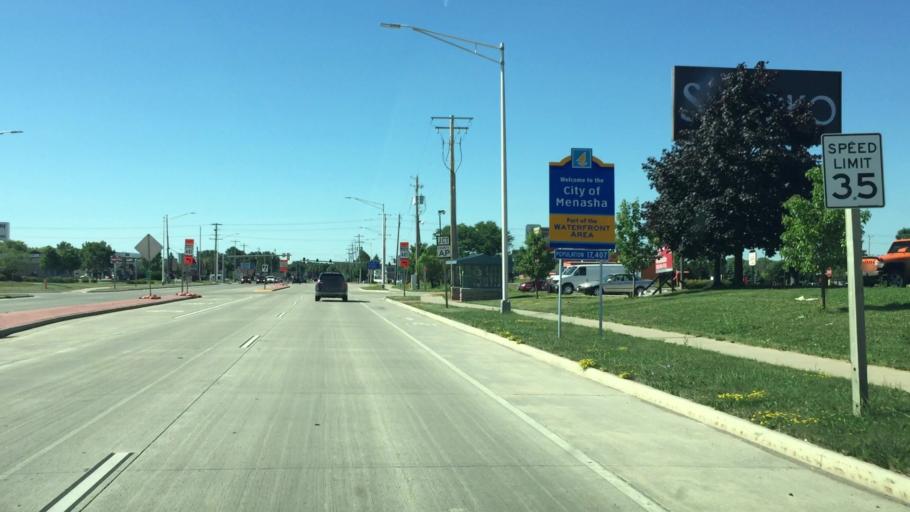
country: US
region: Wisconsin
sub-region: Outagamie County
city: Appleton
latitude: 44.2320
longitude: -88.4242
